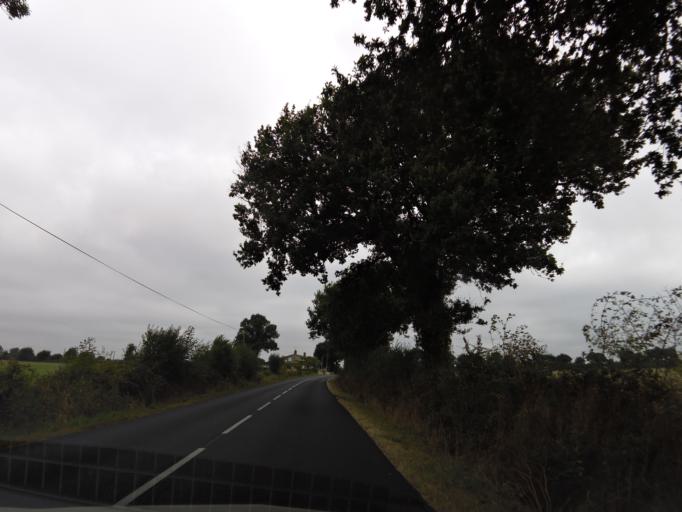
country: FR
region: Pays de la Loire
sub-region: Departement de la Vendee
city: Avrille
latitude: 46.4684
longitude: -1.4511
